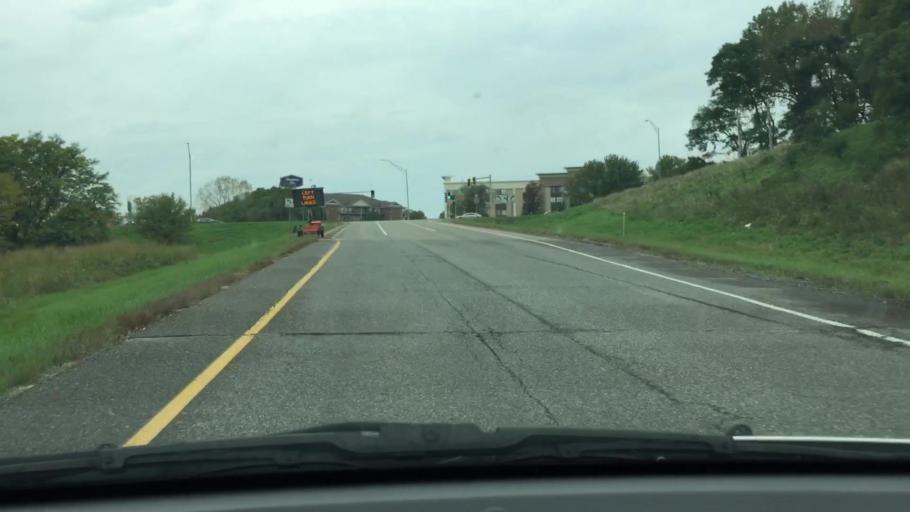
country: US
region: Iowa
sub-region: Johnson County
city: Coralville
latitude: 41.6864
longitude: -91.5628
